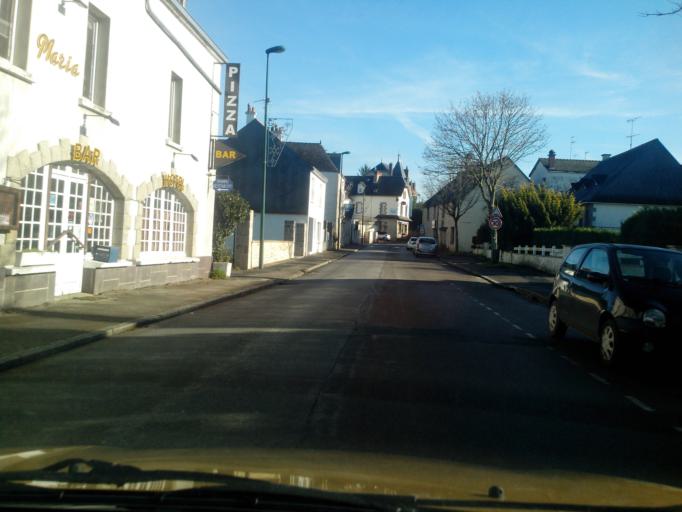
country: FR
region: Brittany
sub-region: Departement du Morbihan
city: Ploermel
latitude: 47.9333
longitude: -2.4053
